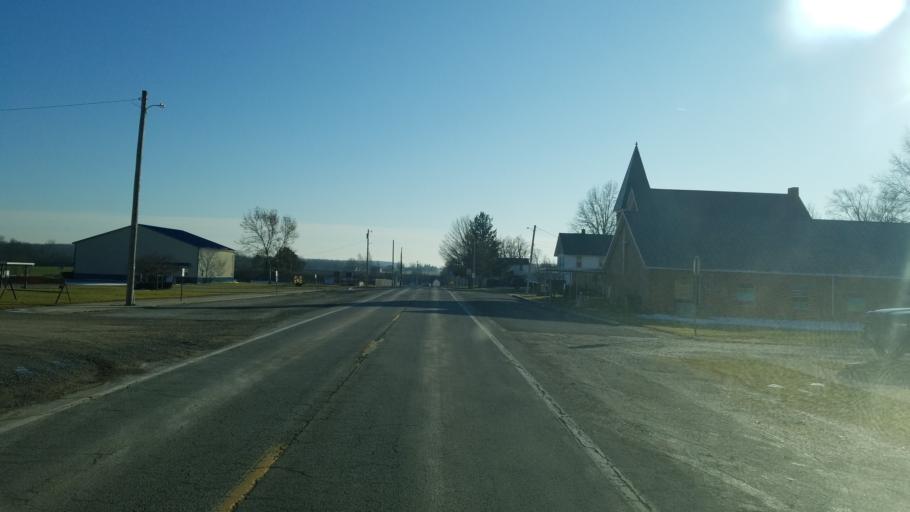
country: US
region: Ohio
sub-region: Sandusky County
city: Green Springs
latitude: 41.1220
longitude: -83.0155
